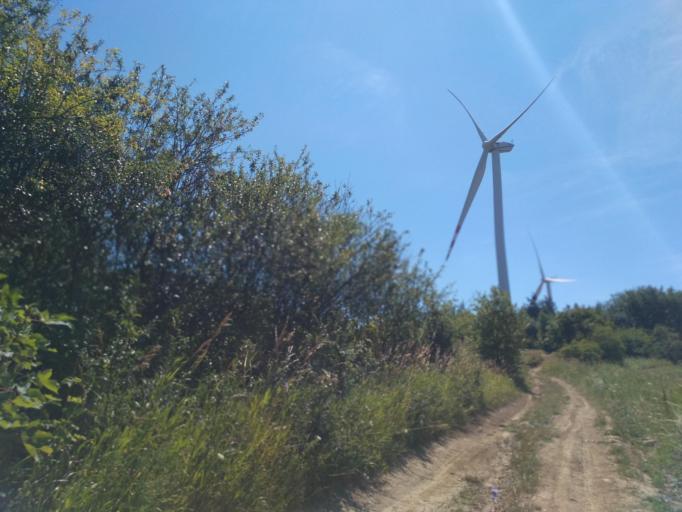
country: PL
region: Subcarpathian Voivodeship
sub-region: Powiat sanocki
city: Bukowsko
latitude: 49.5130
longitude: 22.0546
